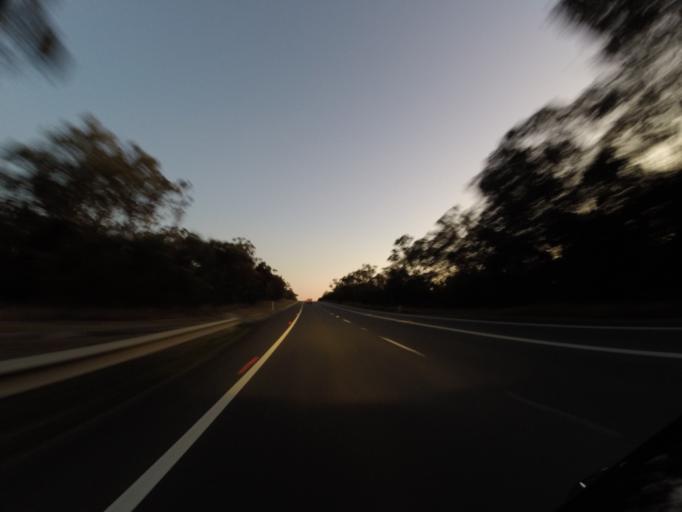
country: AU
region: New South Wales
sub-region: Liverpool
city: Holsworthy
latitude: -34.0304
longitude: 150.9629
